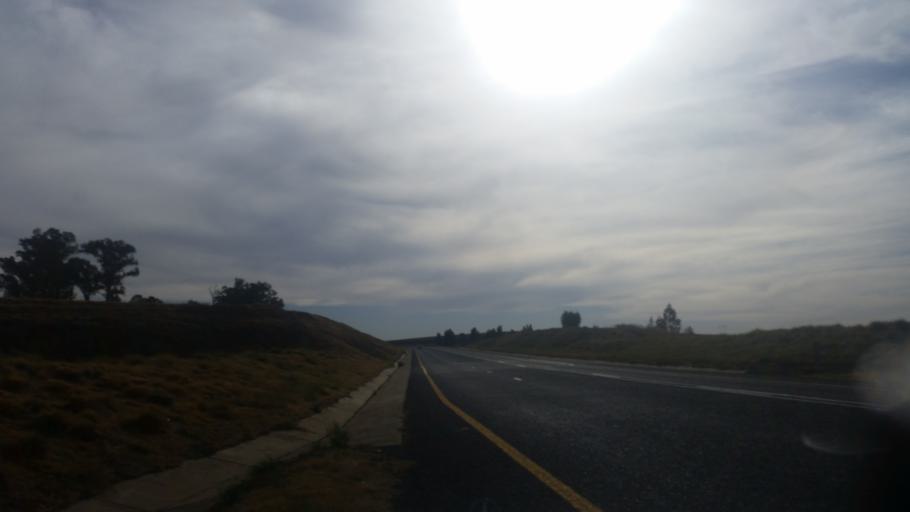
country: ZA
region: Orange Free State
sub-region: Thabo Mofutsanyana District Municipality
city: Phuthaditjhaba
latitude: -28.2716
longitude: 28.8586
